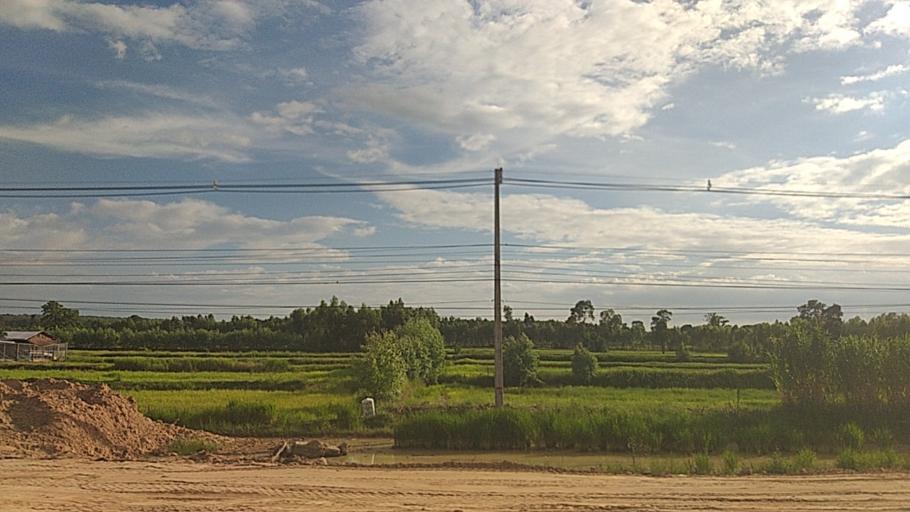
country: TH
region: Surin
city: Kap Choeng
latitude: 14.4865
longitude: 103.5784
